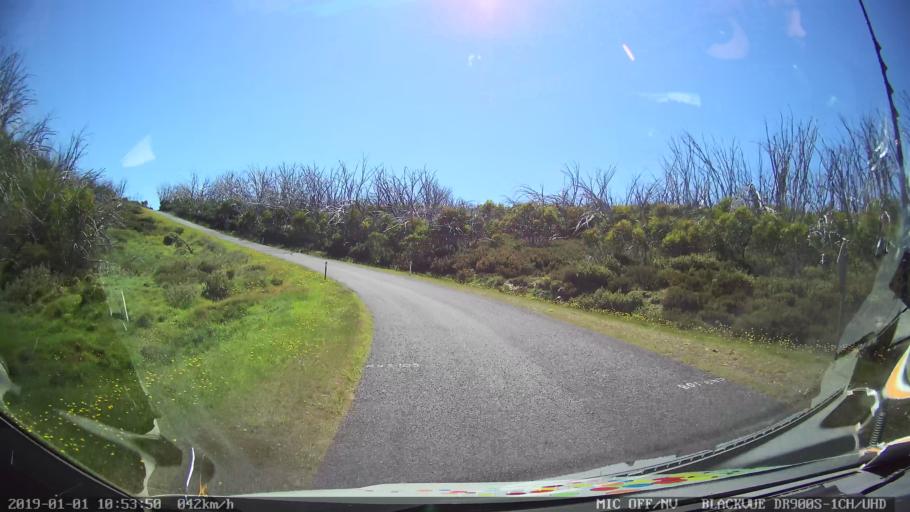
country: AU
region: New South Wales
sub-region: Snowy River
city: Jindabyne
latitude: -36.0117
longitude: 148.3813
